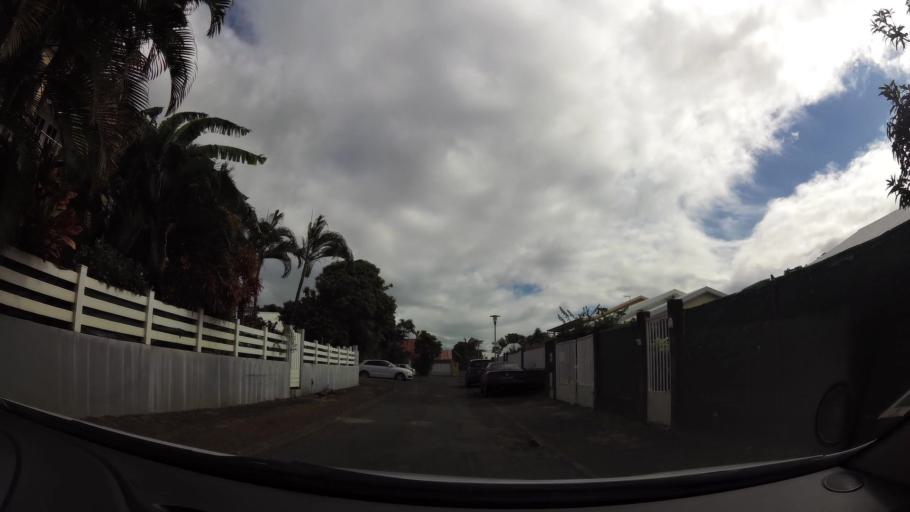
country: RE
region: Reunion
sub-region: Reunion
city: Sainte-Marie
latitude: -20.9028
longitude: 55.5690
